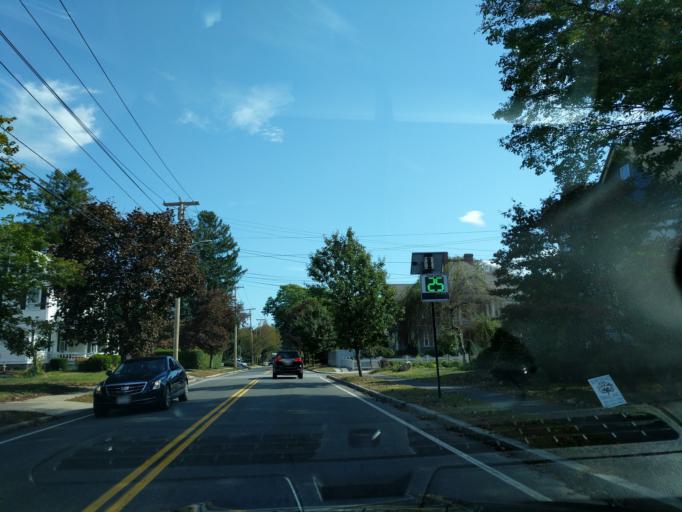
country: US
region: Massachusetts
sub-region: Middlesex County
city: Melrose
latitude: 42.4578
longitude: -71.0562
